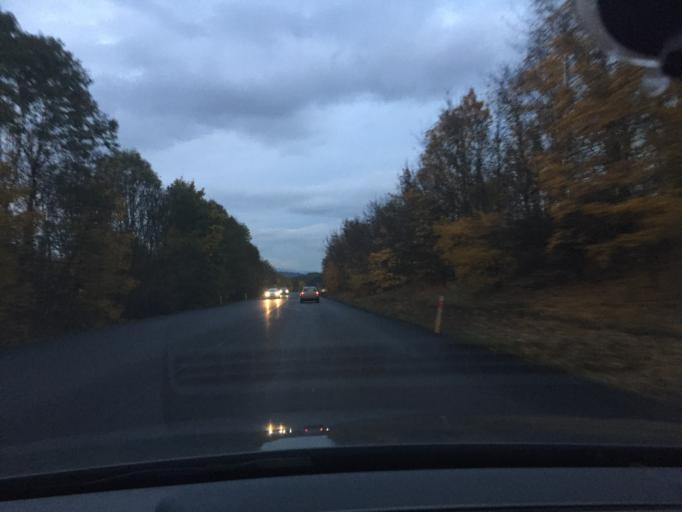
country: CZ
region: Ustecky
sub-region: Okres Teplice
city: Teplice
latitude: 50.6314
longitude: 13.8391
